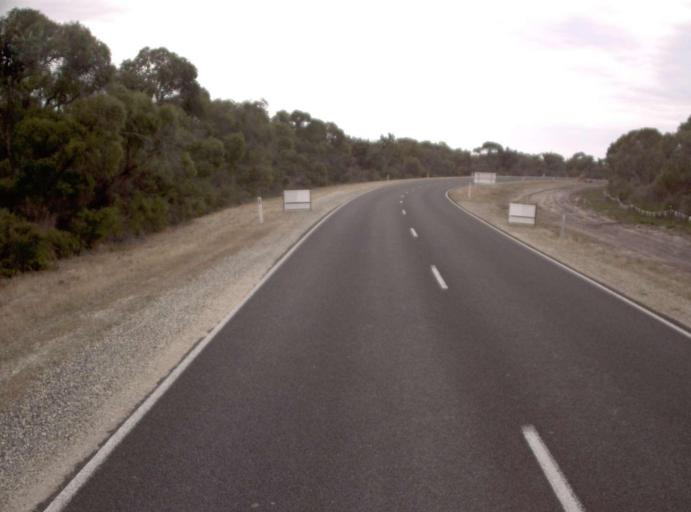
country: AU
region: Victoria
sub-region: East Gippsland
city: Bairnsdale
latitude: -38.1250
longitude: 147.4341
